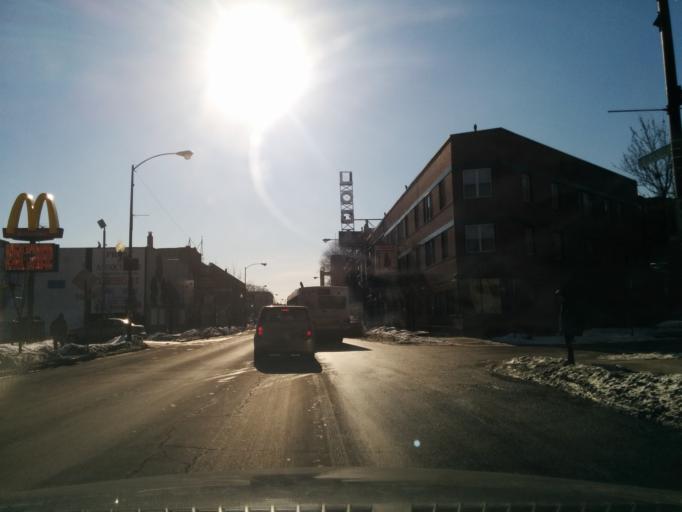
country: US
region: Illinois
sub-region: Cook County
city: Lincolnwood
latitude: 41.9302
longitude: -87.7095
